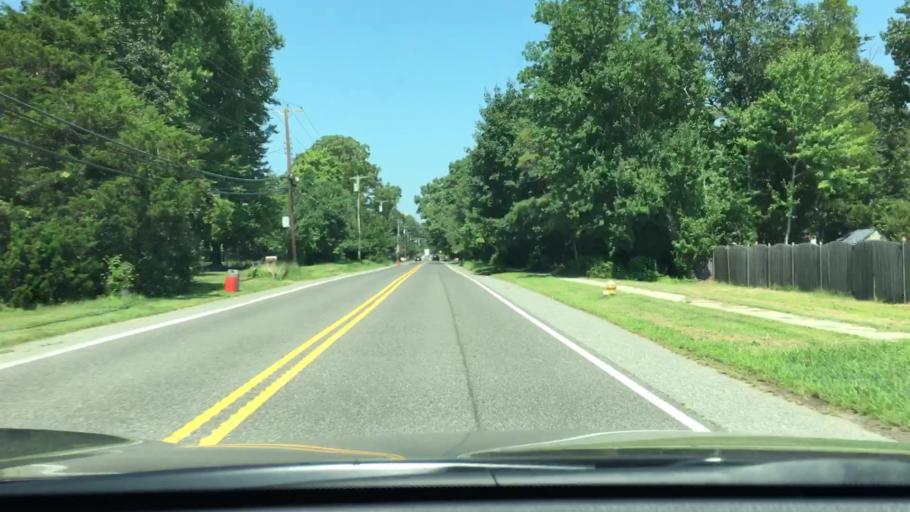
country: US
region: New Jersey
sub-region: Cumberland County
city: Millville
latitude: 39.3823
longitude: -75.0708
